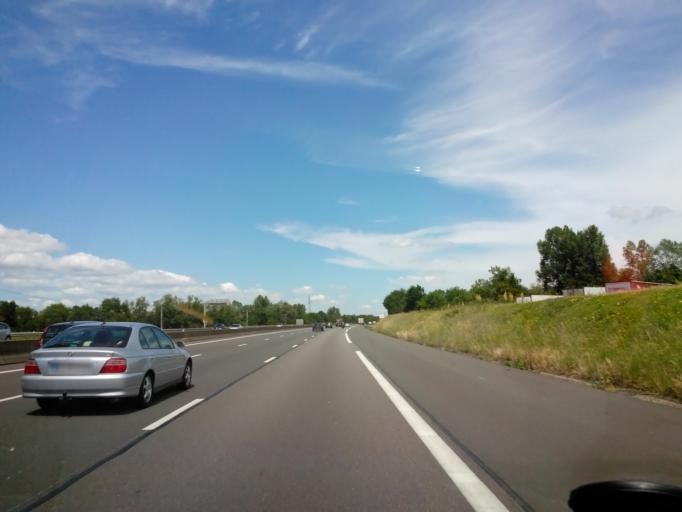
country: FR
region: Rhone-Alpes
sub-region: Departement du Rhone
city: Saint-Georges-de-Reneins
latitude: 46.0432
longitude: 4.7274
